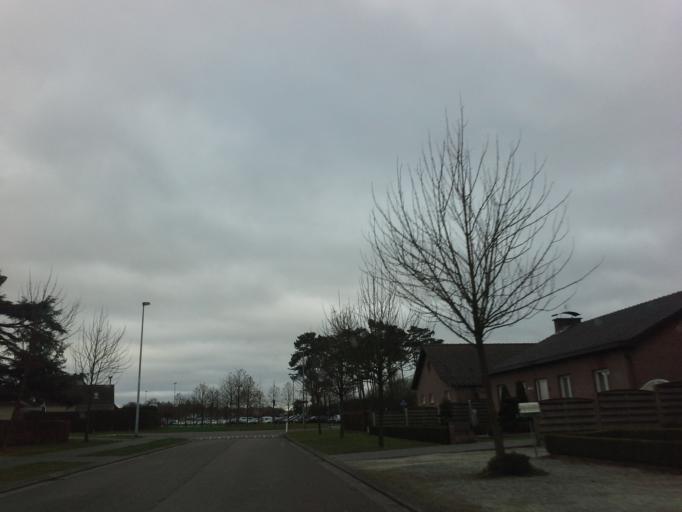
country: BE
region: Flanders
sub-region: Provincie Antwerpen
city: Meerhout
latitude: 51.1306
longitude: 5.0675
